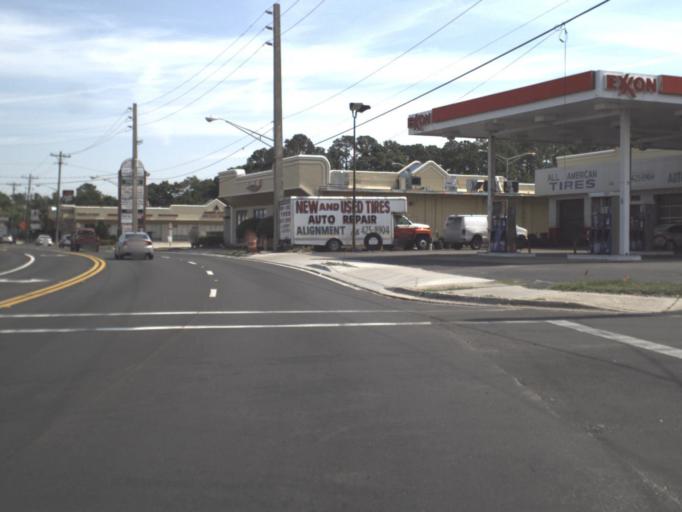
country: US
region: Florida
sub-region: Duval County
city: Jacksonville
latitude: 30.2774
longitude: -81.6030
